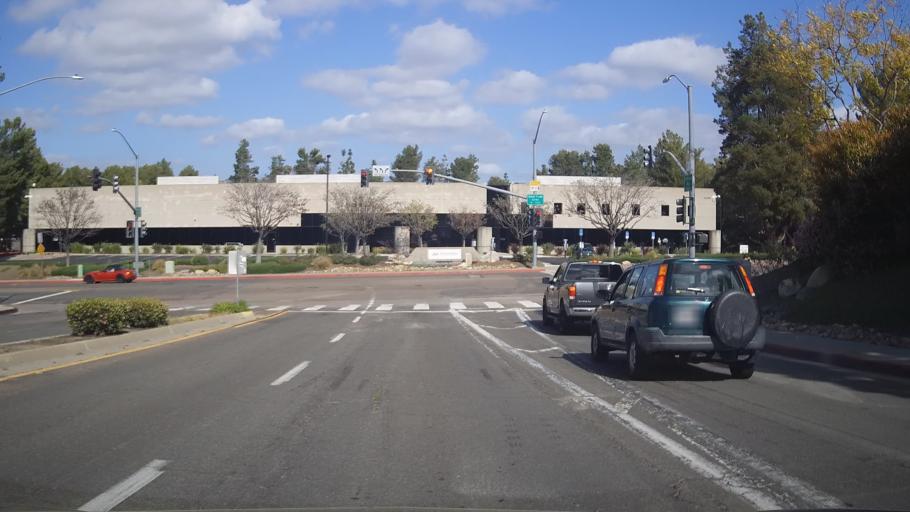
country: US
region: California
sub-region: San Diego County
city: Poway
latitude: 32.9857
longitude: -117.0744
